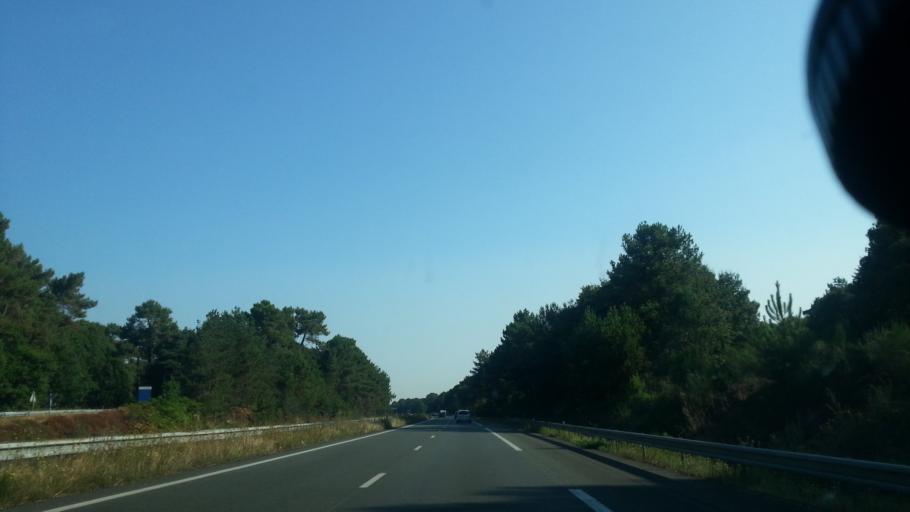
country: FR
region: Poitou-Charentes
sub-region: Departement de la Vienne
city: Chatellerault
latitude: 46.7926
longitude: 0.5098
